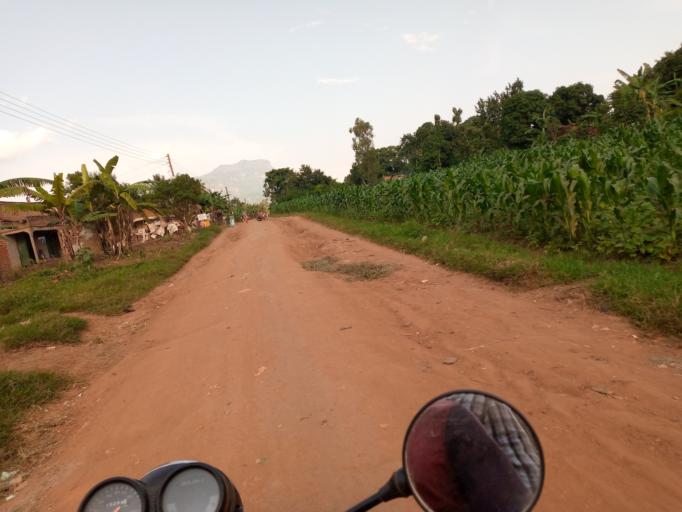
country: UG
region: Eastern Region
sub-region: Mbale District
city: Mbale
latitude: 1.0545
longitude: 34.1642
